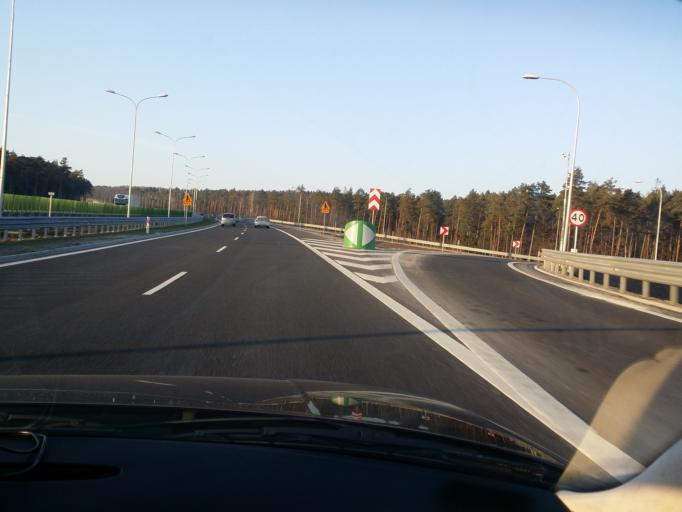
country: PL
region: Swietokrzyskie
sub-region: Powiat skarzyski
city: Skarzysko-Kamienna
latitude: 51.1194
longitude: 20.8476
